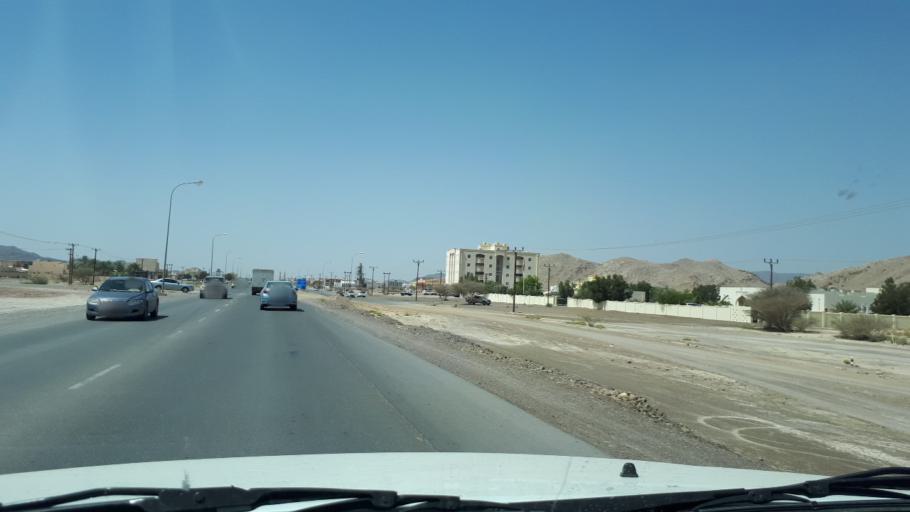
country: OM
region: Muhafazat ad Dakhiliyah
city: Bahla'
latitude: 23.0178
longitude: 57.3288
